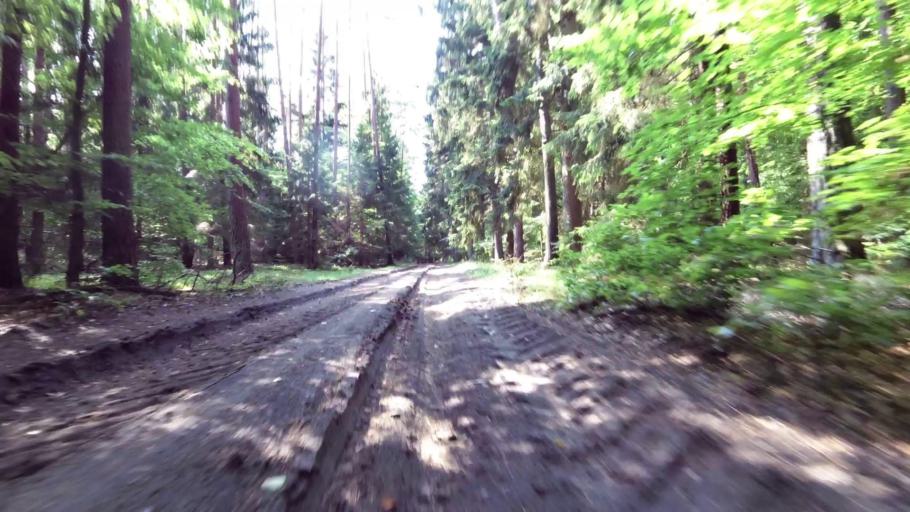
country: PL
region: West Pomeranian Voivodeship
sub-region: Powiat kamienski
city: Miedzyzdroje
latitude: 53.9136
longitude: 14.4923
